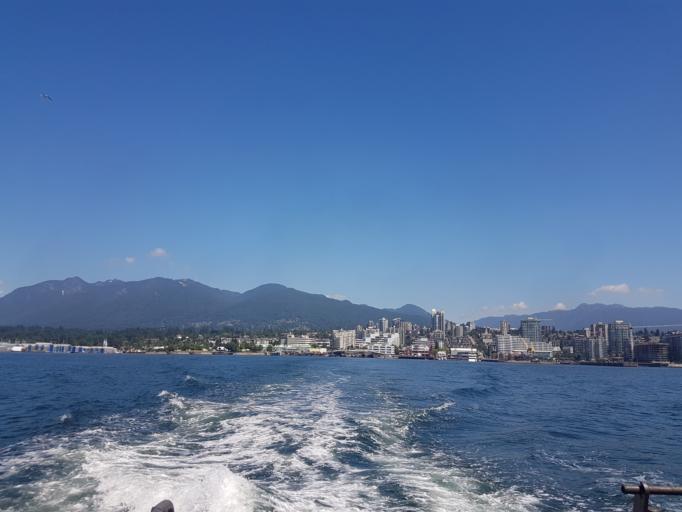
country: CA
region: British Columbia
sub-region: Fraser Valley Regional District
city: North Vancouver
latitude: 49.3040
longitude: -123.0876
